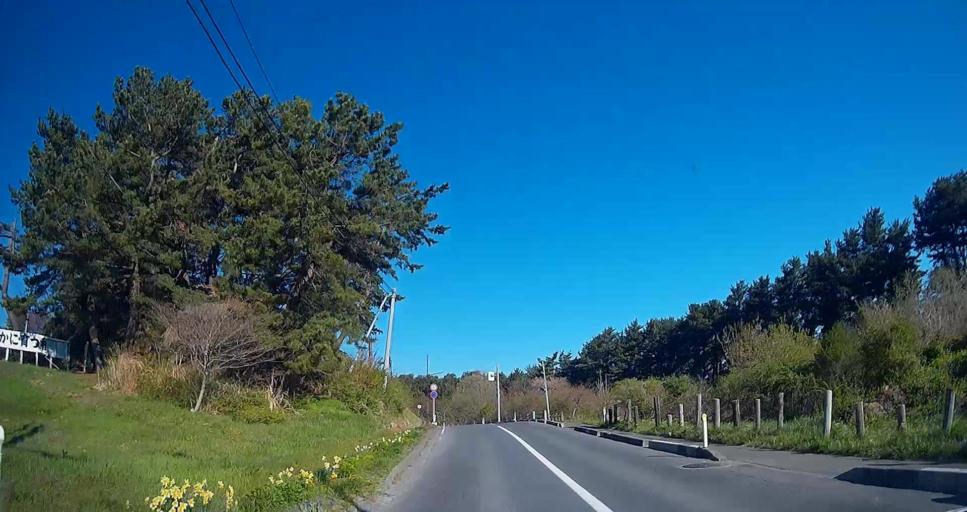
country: JP
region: Aomori
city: Hachinohe
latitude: 40.5142
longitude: 141.6046
